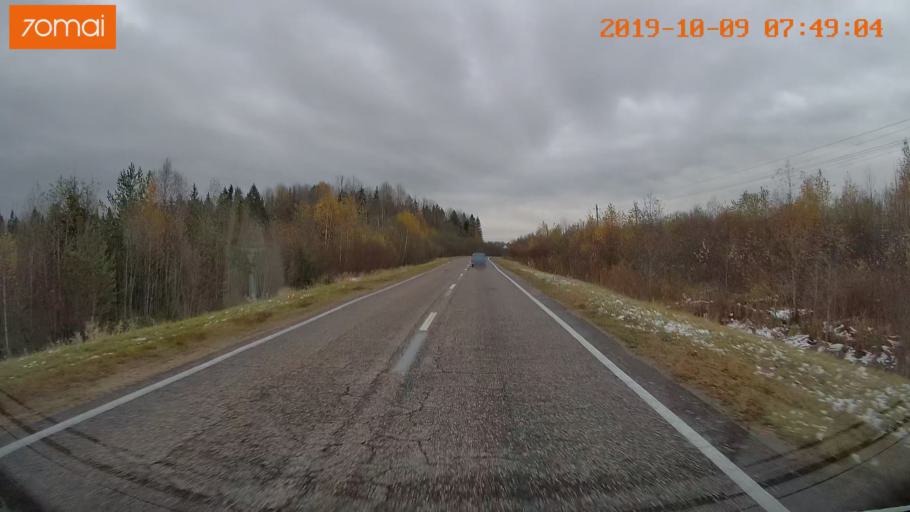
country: RU
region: Jaroslavl
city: Kukoboy
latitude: 58.6672
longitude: 39.8390
